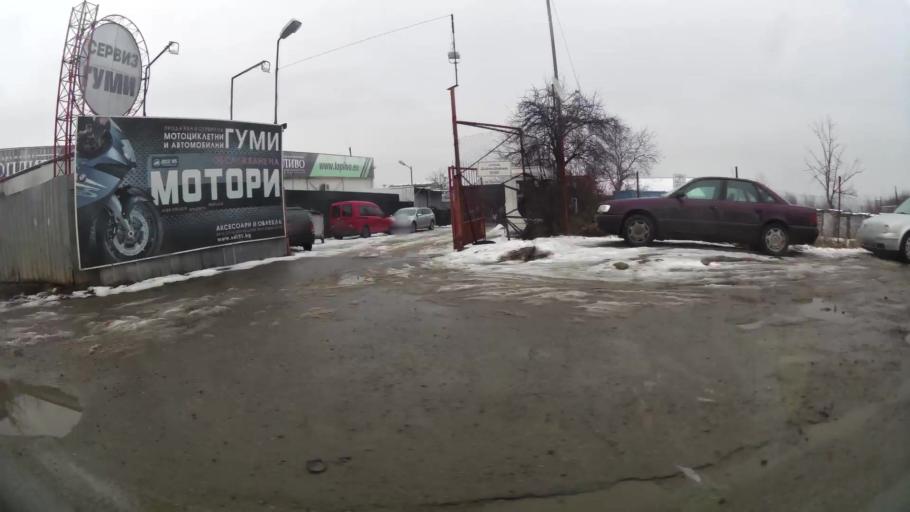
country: BG
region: Sofiya
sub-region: Obshtina Bozhurishte
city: Bozhurishte
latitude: 42.6870
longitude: 23.2330
